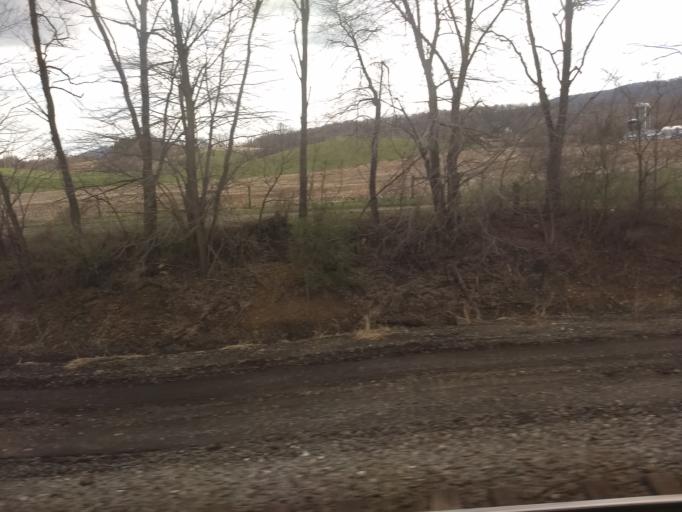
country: US
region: Pennsylvania
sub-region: Mifflin County
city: Lewistown
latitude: 40.5789
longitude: -77.5887
